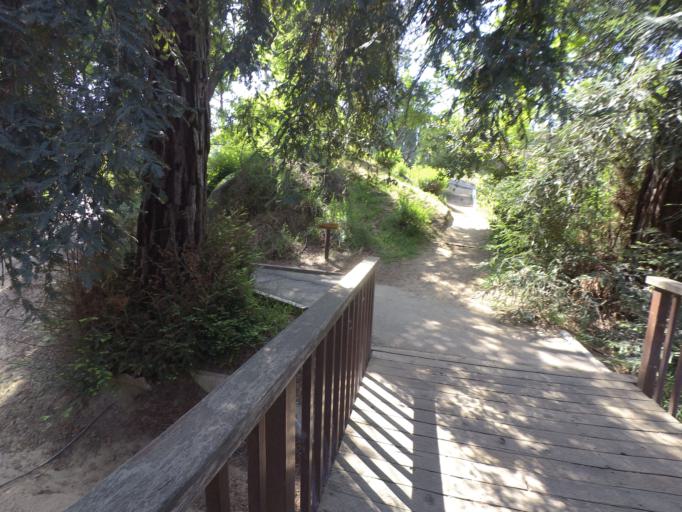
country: US
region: California
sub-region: Riverside County
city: Highgrove
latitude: 33.9715
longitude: -117.3189
